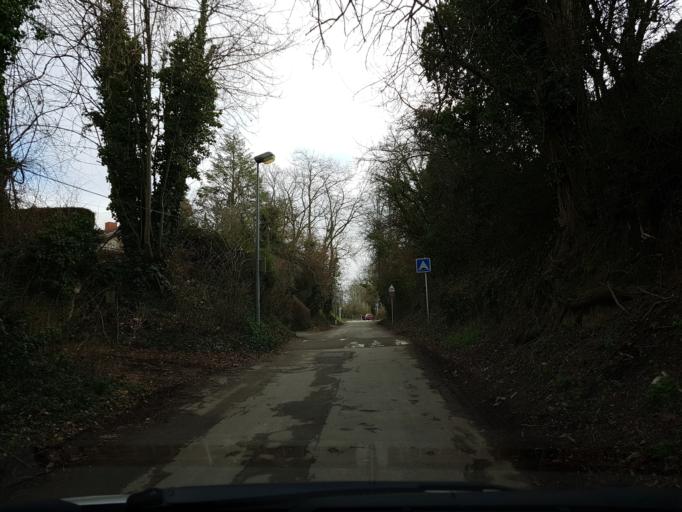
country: FR
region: Alsace
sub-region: Departement du Haut-Rhin
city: Riedisheim
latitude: 47.7478
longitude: 7.3733
